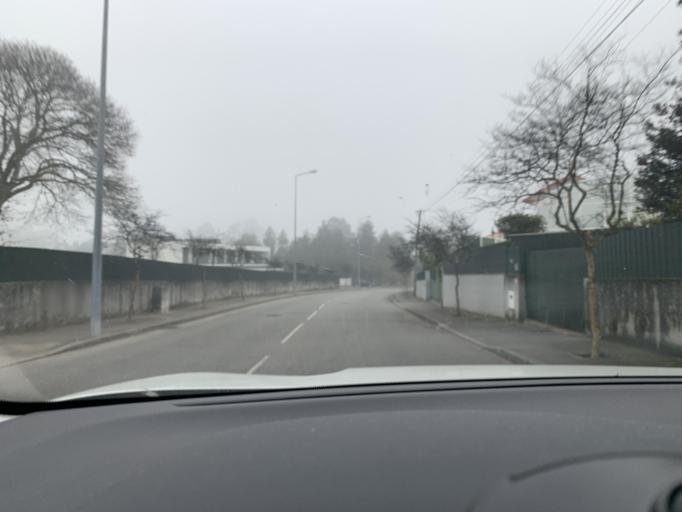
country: PT
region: Viseu
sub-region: Viseu
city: Viseu
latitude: 40.6370
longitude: -7.9190
